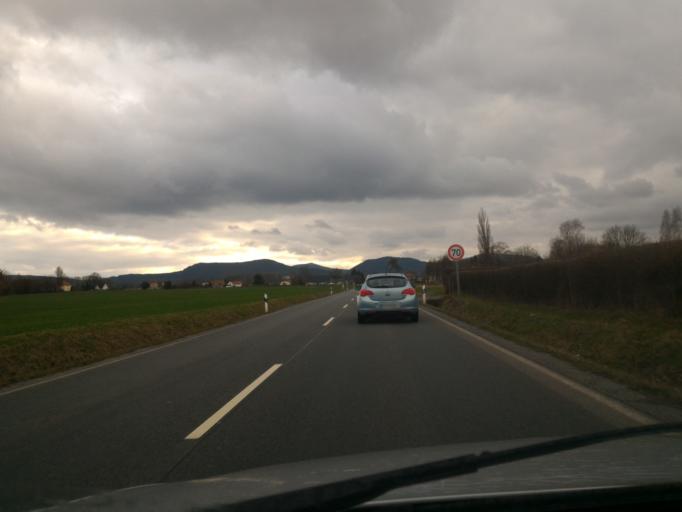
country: DE
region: Saxony
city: Zittau
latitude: 50.8882
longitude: 14.7924
